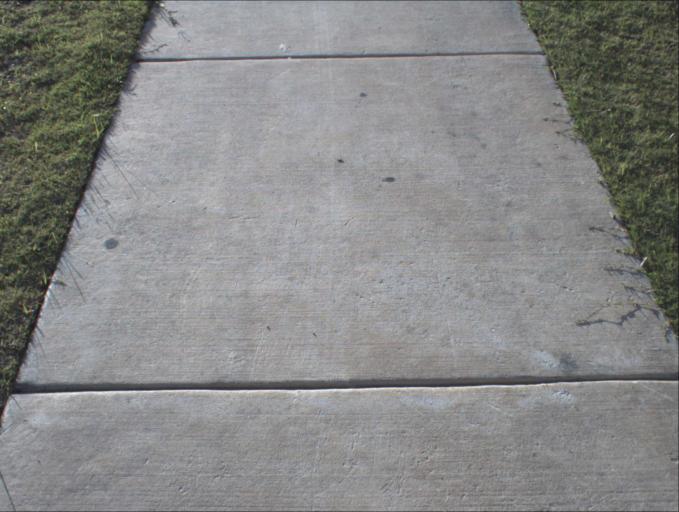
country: AU
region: Queensland
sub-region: Logan
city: North Maclean
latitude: -27.8025
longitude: 152.9609
